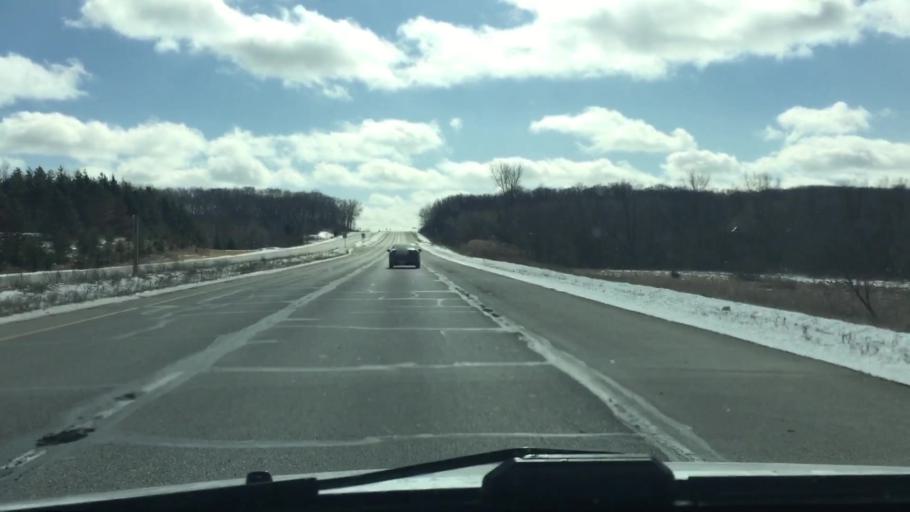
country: US
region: Wisconsin
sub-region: Waukesha County
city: Big Bend
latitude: 42.9429
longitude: -88.2284
